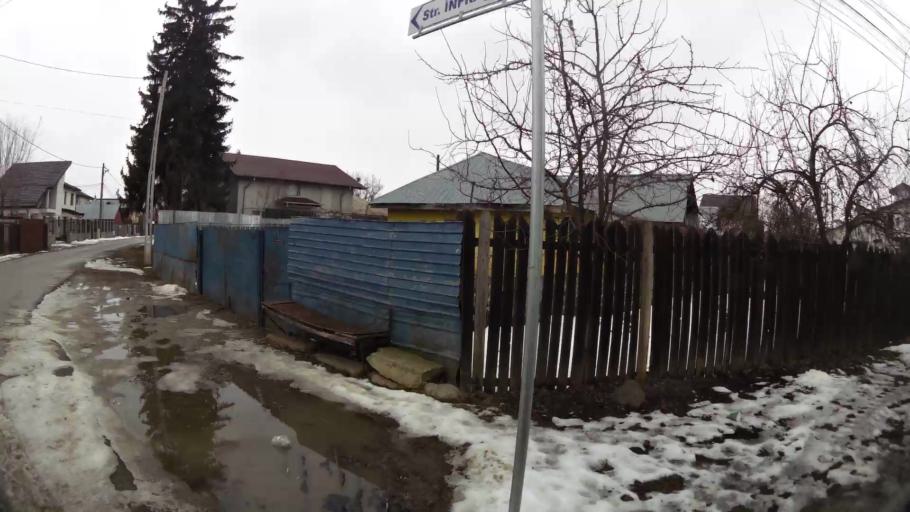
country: RO
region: Ilfov
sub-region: Comuna Tunari
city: Tunari
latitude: 44.5443
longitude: 26.1327
